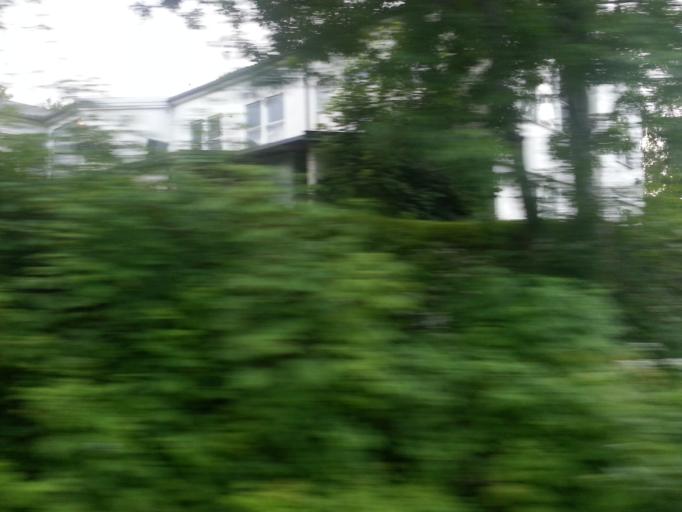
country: NO
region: Sor-Trondelag
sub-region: Trondheim
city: Trondheim
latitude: 63.4350
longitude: 10.4933
